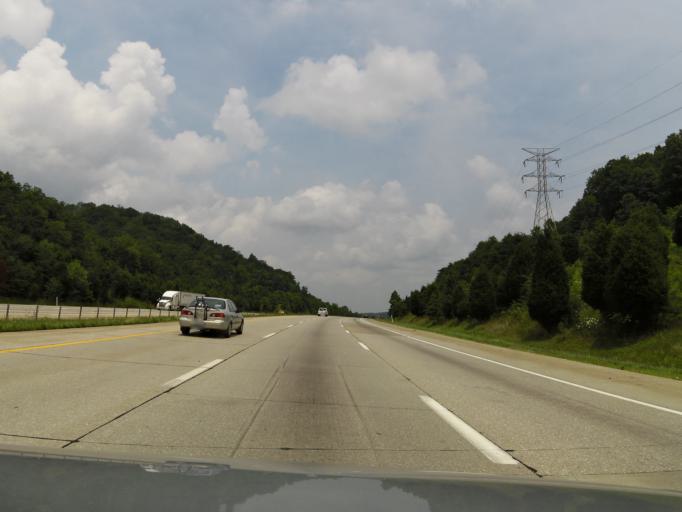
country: US
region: Kentucky
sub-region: Bullitt County
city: Lebanon Junction
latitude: 37.8785
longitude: -85.7022
